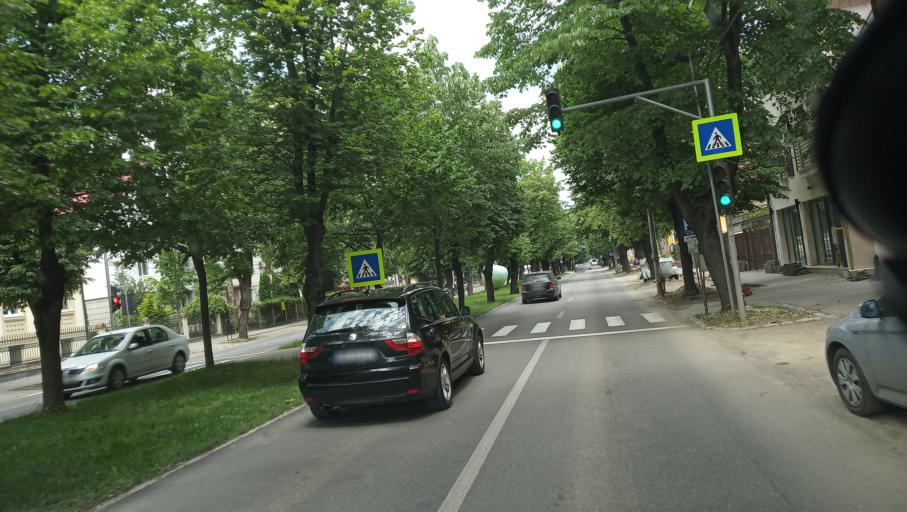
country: RO
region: Bistrita-Nasaud
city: Bistrita
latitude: 47.1330
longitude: 24.4932
